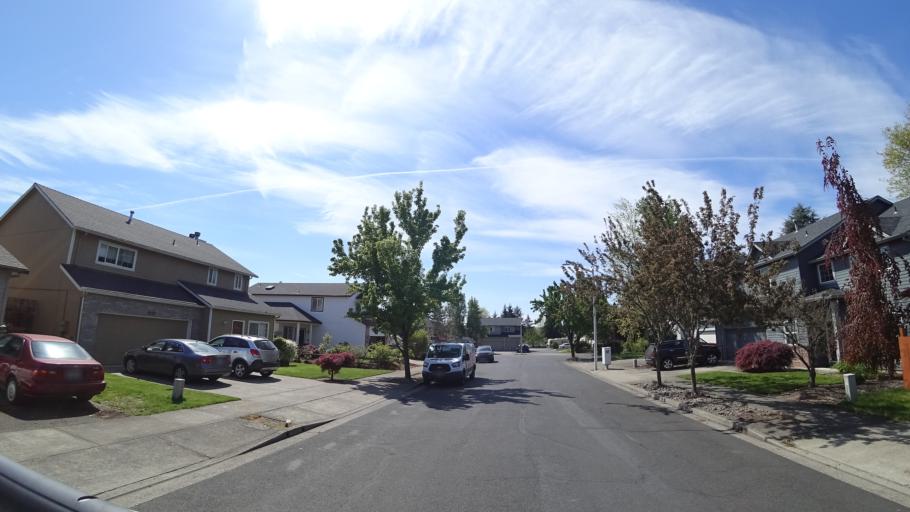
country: US
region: Oregon
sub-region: Washington County
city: Hillsboro
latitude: 45.5081
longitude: -122.9541
